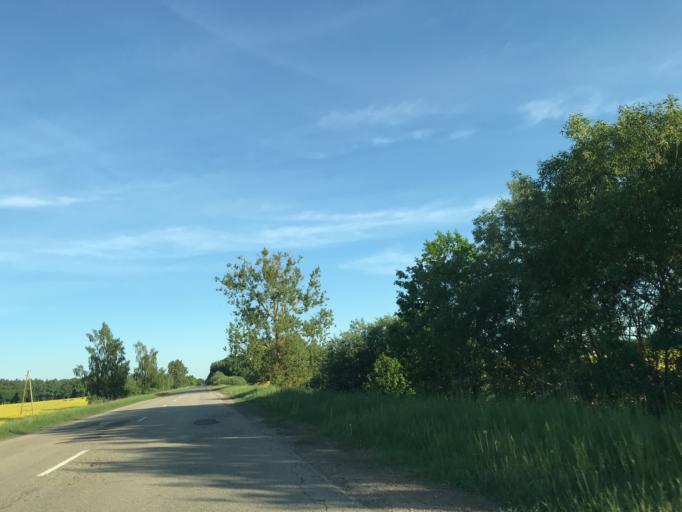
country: LV
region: Ozolnieku
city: Ozolnieki
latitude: 56.6013
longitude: 23.9506
